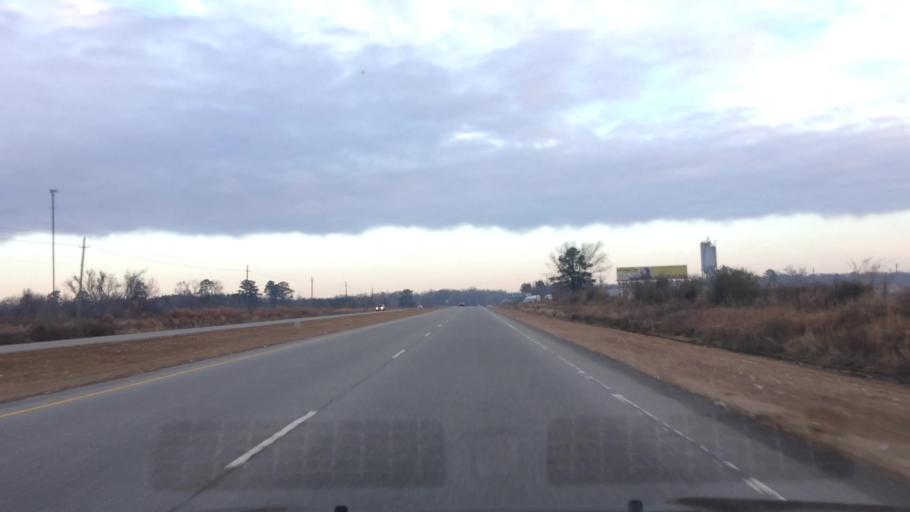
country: US
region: North Carolina
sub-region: Pitt County
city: Ayden
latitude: 35.4853
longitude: -77.4311
